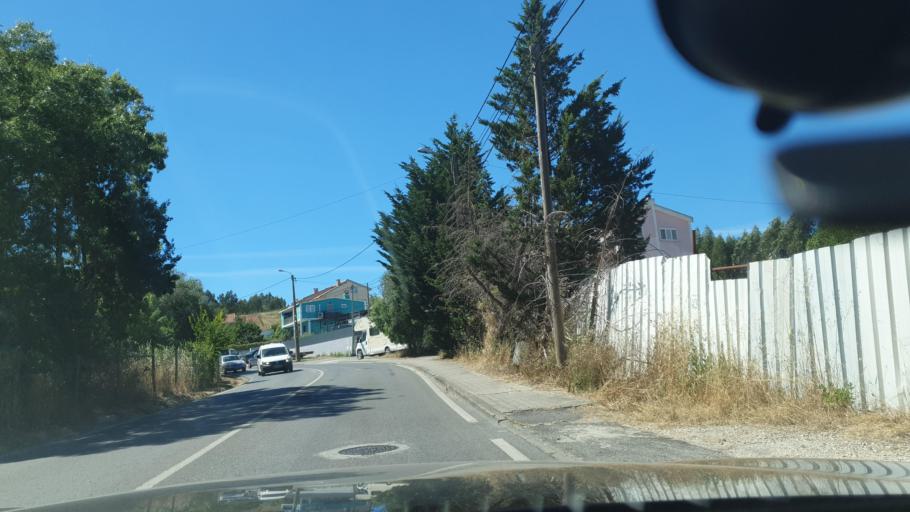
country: PT
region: Lisbon
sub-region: Sintra
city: Belas
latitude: 38.7823
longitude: -9.2539
